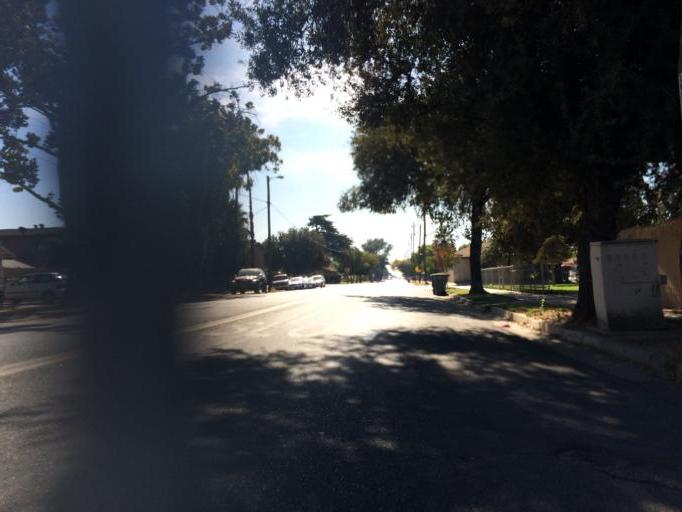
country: US
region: California
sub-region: Fresno County
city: Fresno
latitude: 36.7323
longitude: -119.7637
